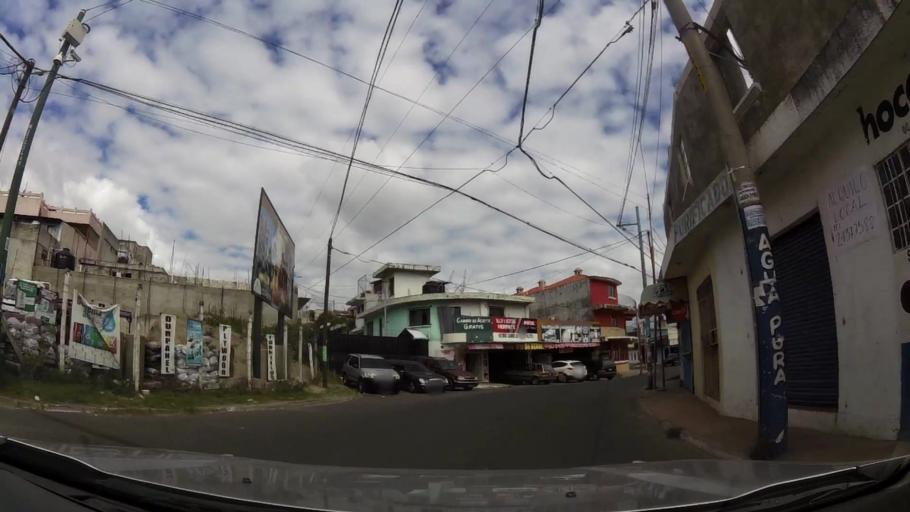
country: GT
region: Guatemala
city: Guatemala City
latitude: 14.6767
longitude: -90.5472
